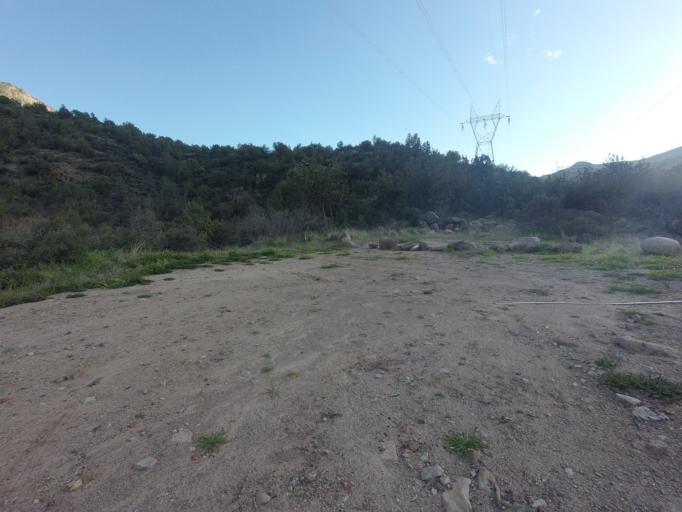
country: US
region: Arizona
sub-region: Gila County
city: Pine
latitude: 34.3880
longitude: -111.6553
